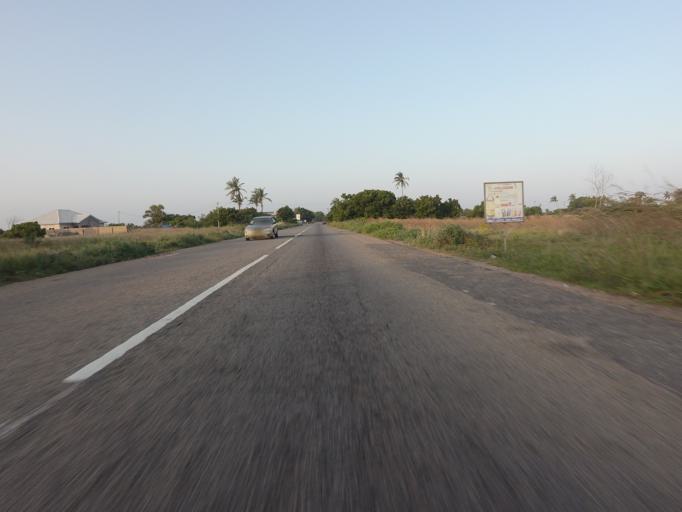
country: GH
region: Volta
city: Anloga
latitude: 5.7870
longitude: 0.8569
